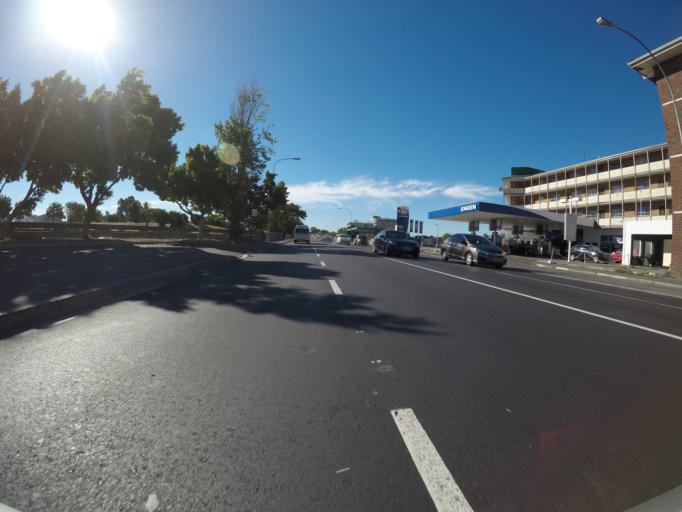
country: ZA
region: Western Cape
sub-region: City of Cape Town
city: Kraaifontein
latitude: -33.9214
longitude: 18.6760
